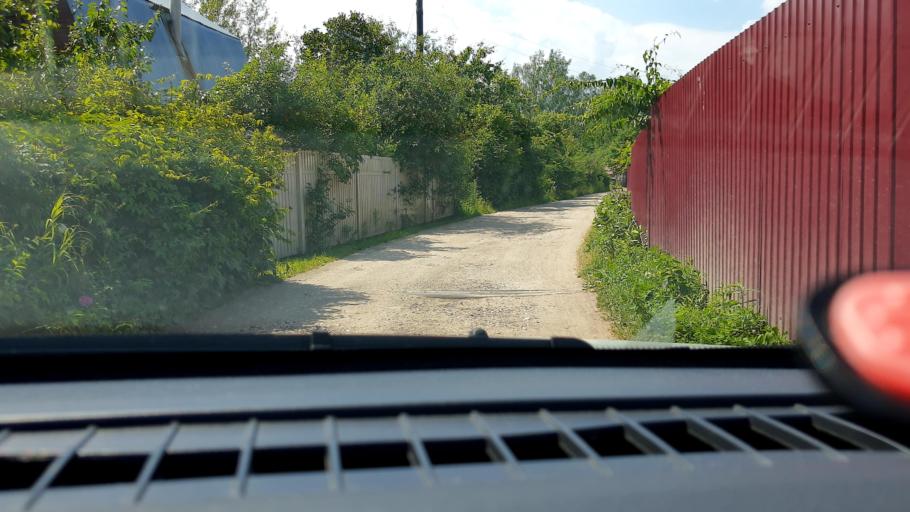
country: RU
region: Nizjnij Novgorod
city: Neklyudovo
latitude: 56.4508
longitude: 43.9954
